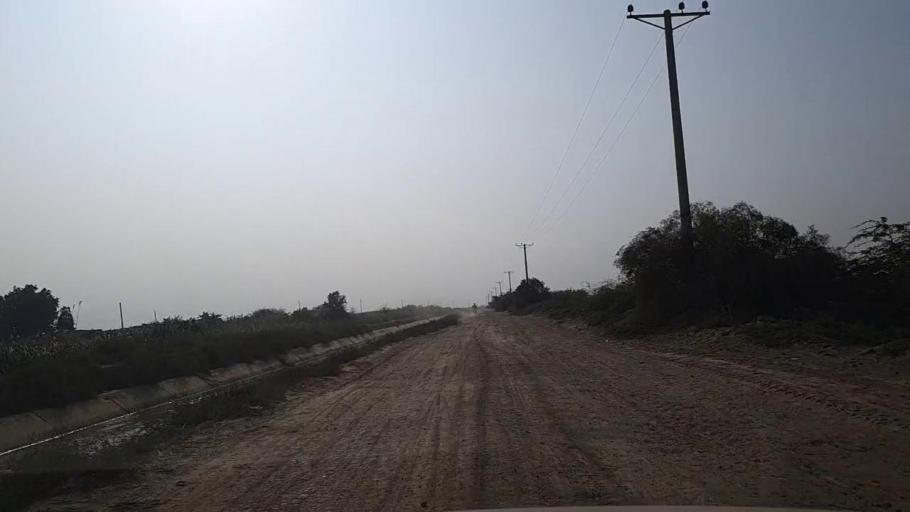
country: PK
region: Sindh
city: Keti Bandar
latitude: 24.1984
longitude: 67.6201
